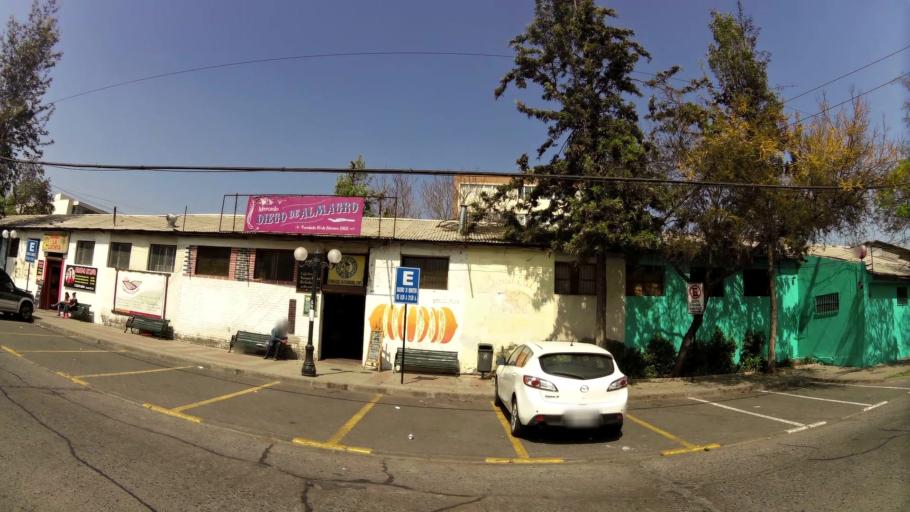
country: CL
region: Santiago Metropolitan
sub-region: Provincia de Santiago
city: Villa Presidente Frei, Nunoa, Santiago, Chile
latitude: -33.4415
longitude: -70.5993
